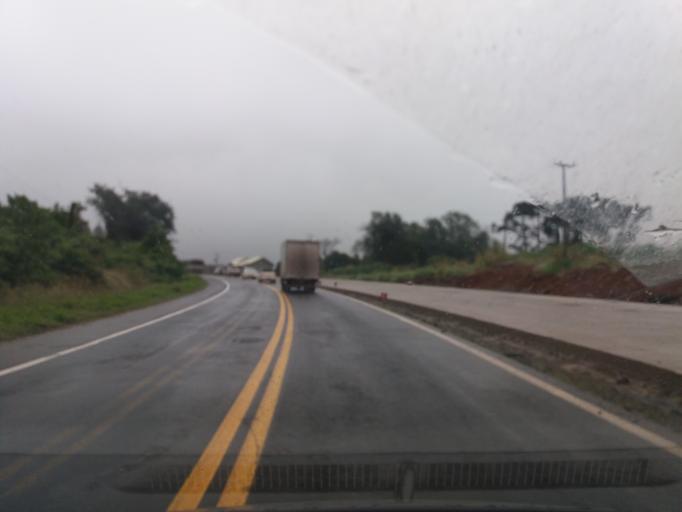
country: BR
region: Parana
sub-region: Realeza
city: Realeza
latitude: -25.4682
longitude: -53.5818
